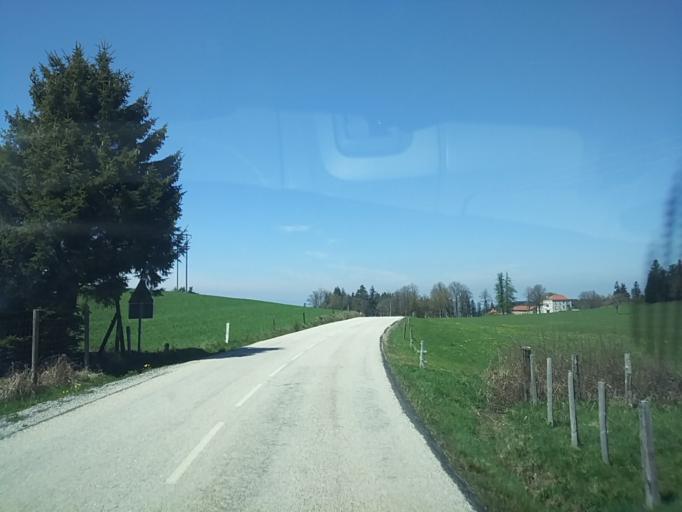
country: FR
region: Auvergne
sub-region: Departement de la Haute-Loire
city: Saint-Just-Malmont
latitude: 45.3234
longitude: 4.3338
